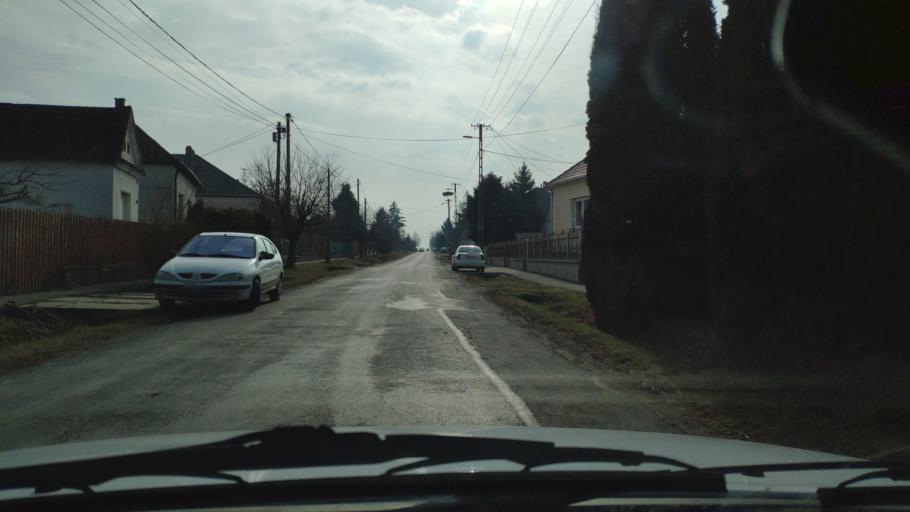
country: HU
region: Zala
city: Nagykanizsa
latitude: 46.4541
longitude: 16.9141
